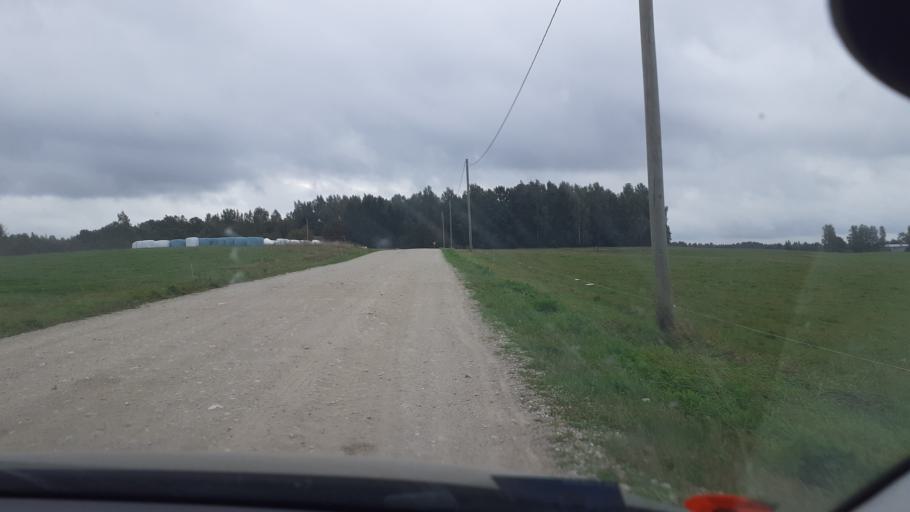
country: LV
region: Alsunga
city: Alsunga
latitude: 56.8969
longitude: 21.6890
